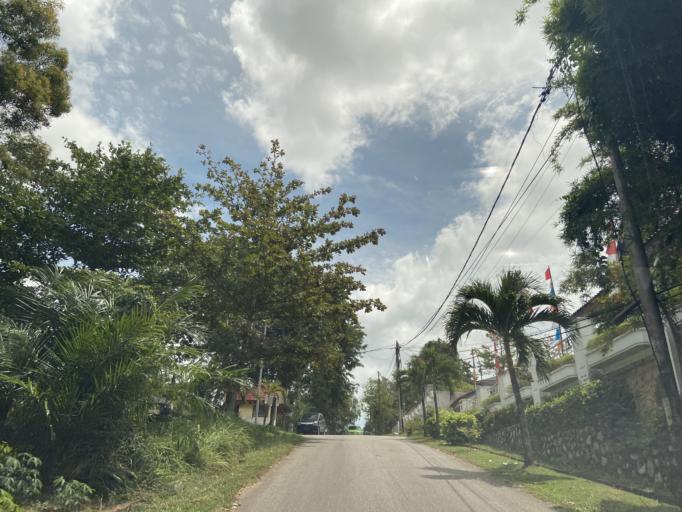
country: SG
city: Singapore
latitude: 1.1523
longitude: 104.0138
